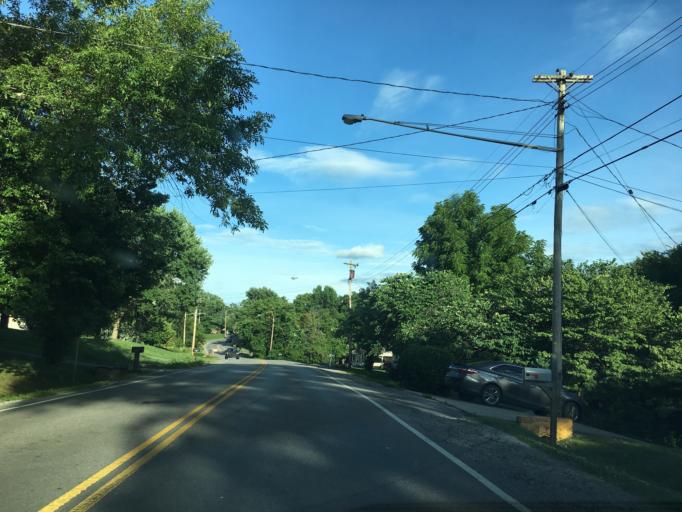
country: US
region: Tennessee
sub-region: Davidson County
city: Oak Hill
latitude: 36.0662
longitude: -86.7294
